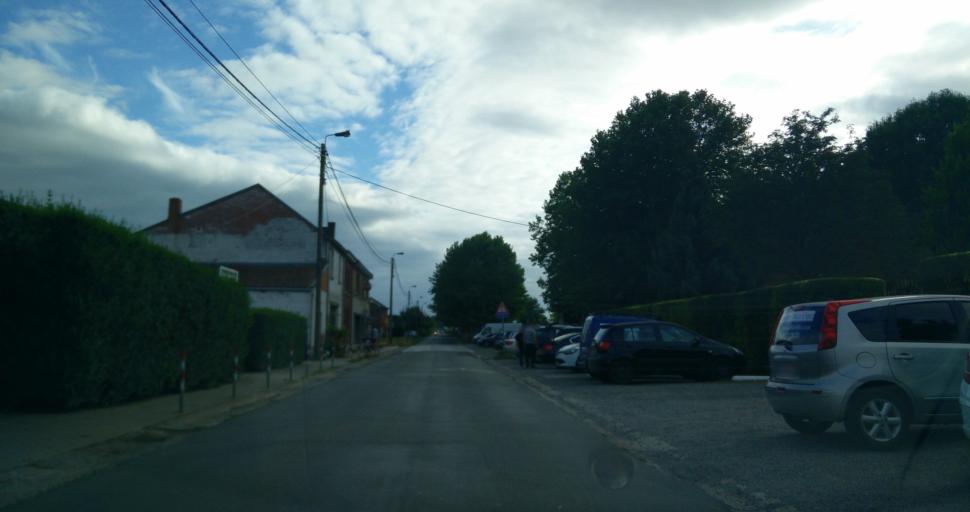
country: BE
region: Wallonia
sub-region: Province de Liege
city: Blegny
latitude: 50.6881
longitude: 5.7244
